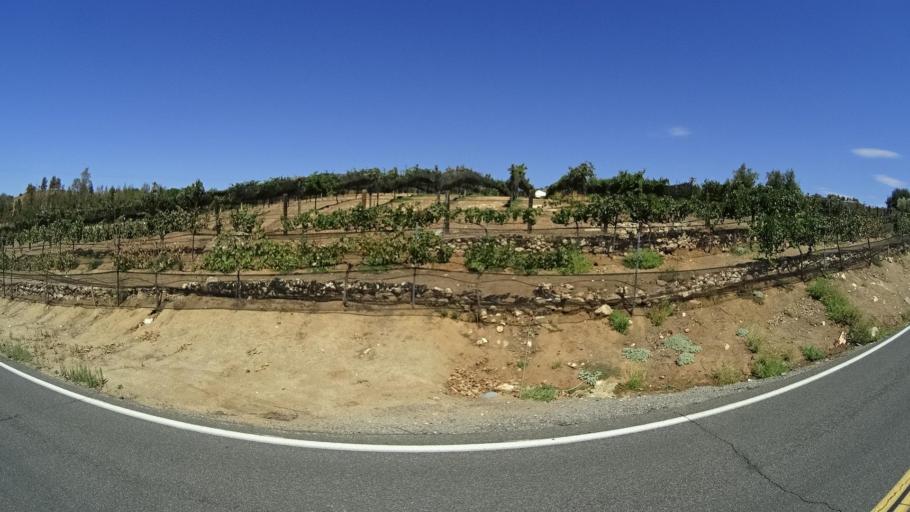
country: US
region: California
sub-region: San Diego County
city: San Diego Country Estates
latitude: 33.0507
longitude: -116.7827
